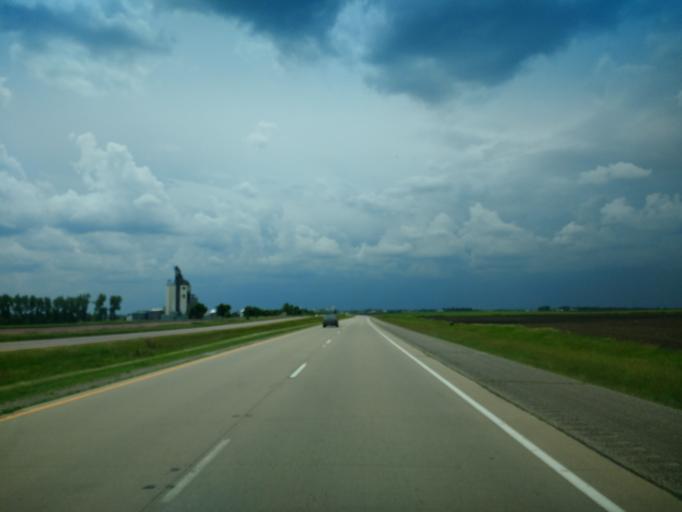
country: US
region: Minnesota
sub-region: Nobles County
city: Worthington
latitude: 43.6558
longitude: -95.5382
